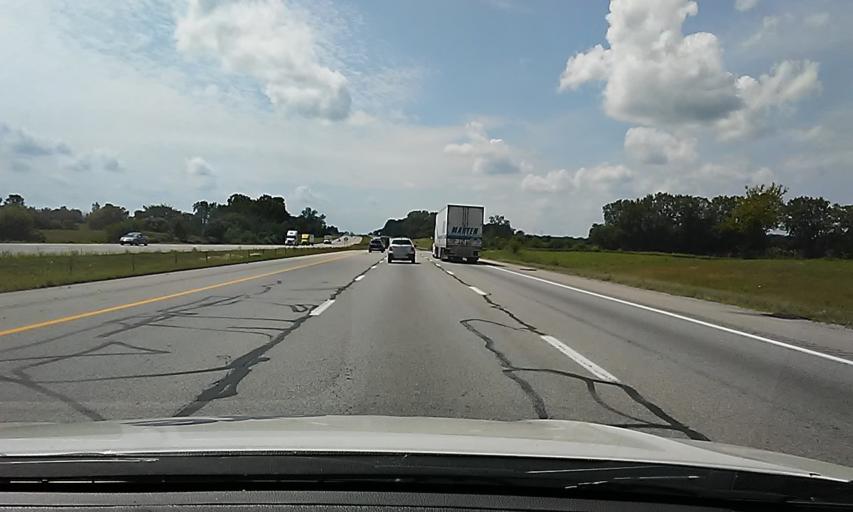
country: US
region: Ohio
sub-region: Madison County
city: Choctaw Lake
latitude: 39.9378
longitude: -83.5708
